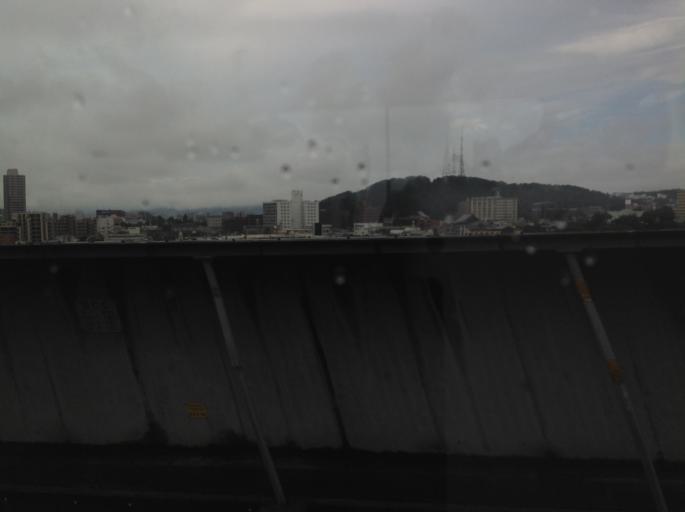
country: JP
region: Miyagi
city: Sendai
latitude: 38.2481
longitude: 140.8911
